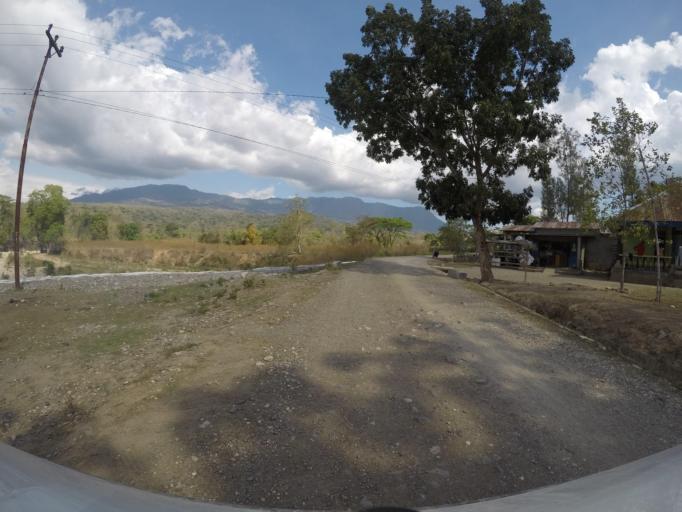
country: TL
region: Bobonaro
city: Maliana
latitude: -8.9989
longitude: 125.1966
